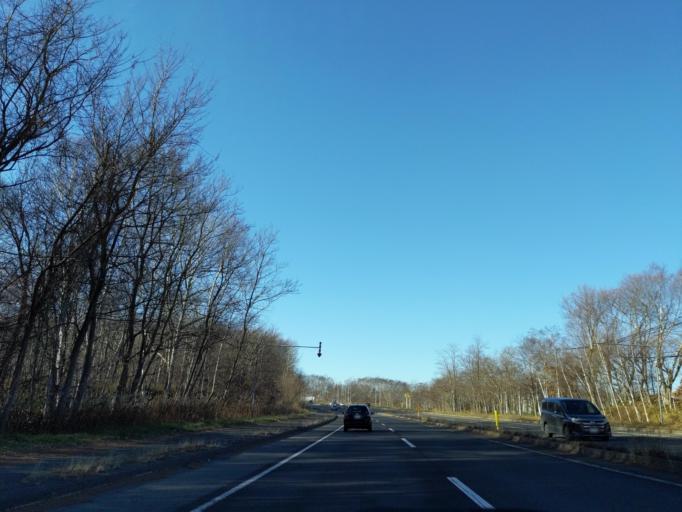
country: JP
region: Hokkaido
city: Kitahiroshima
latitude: 42.9345
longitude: 141.5235
